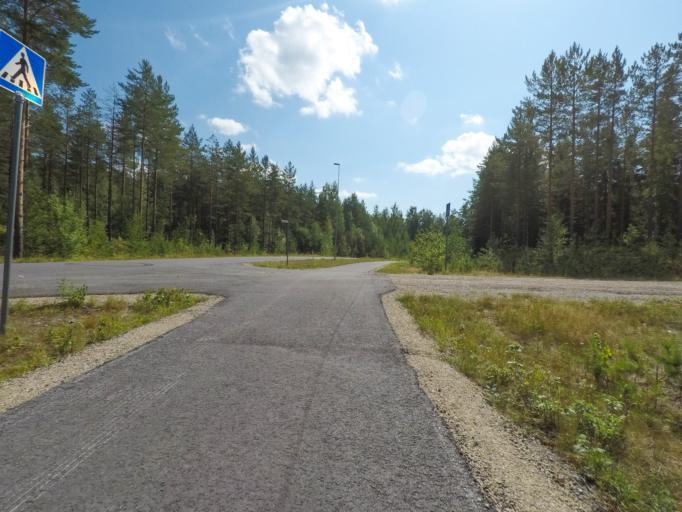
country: FI
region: Southern Savonia
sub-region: Mikkeli
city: Puumala
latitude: 61.5092
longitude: 28.1685
